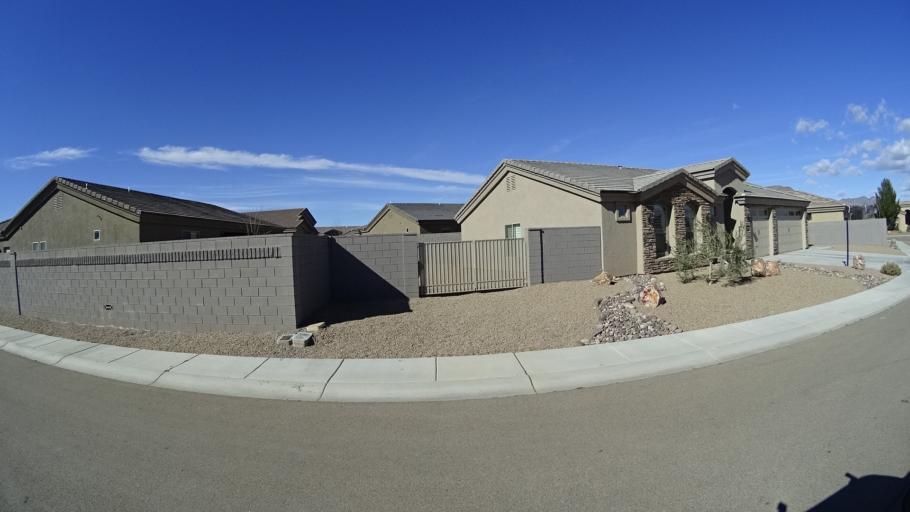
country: US
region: Arizona
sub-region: Mohave County
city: New Kingman-Butler
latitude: 35.2338
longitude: -114.0213
